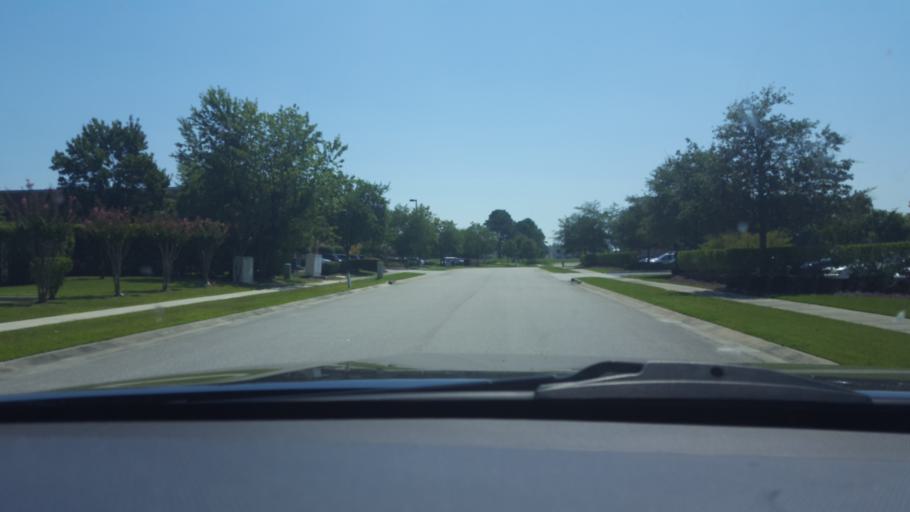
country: US
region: North Carolina
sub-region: New Hanover County
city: Ogden
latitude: 34.2417
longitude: -77.8254
